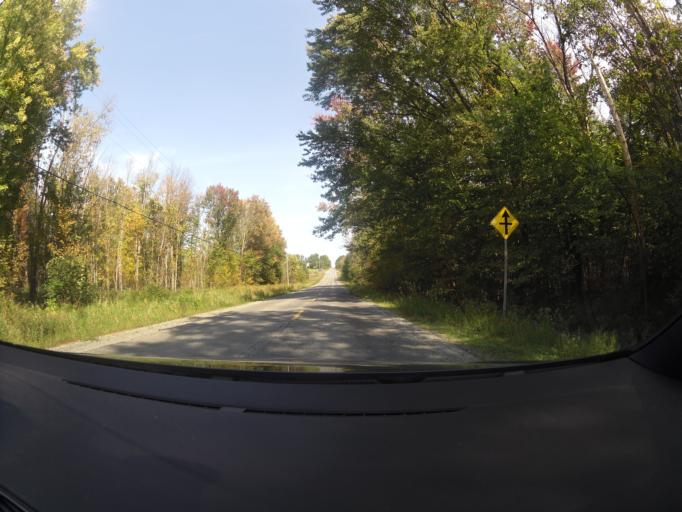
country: CA
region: Ontario
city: Bells Corners
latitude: 45.4362
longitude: -75.9969
